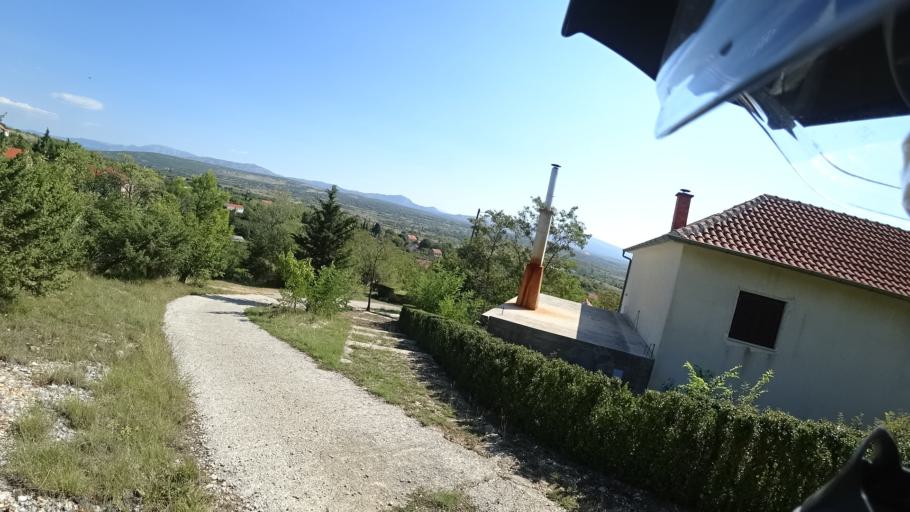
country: HR
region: Sibensko-Kniniska
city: Drnis
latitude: 43.8780
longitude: 16.1981
